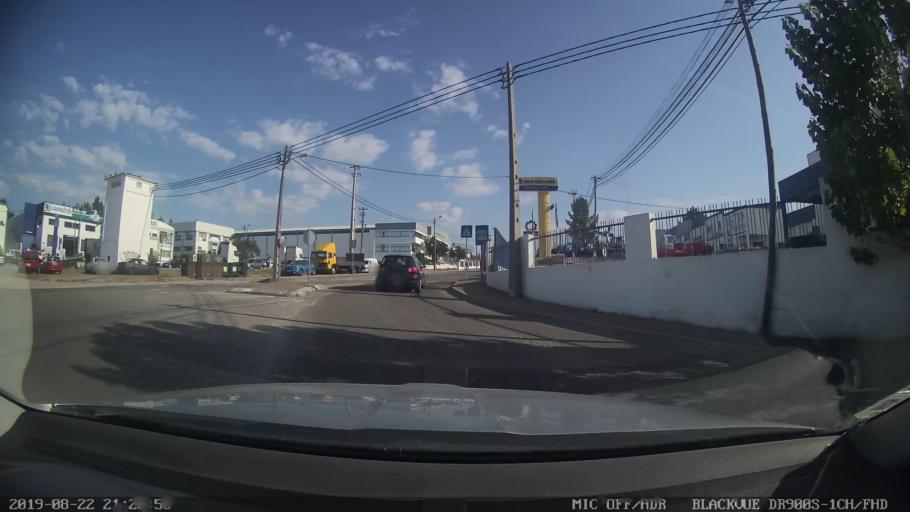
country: PT
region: Castelo Branco
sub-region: Serta
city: Serta
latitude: 39.8156
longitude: -8.1089
